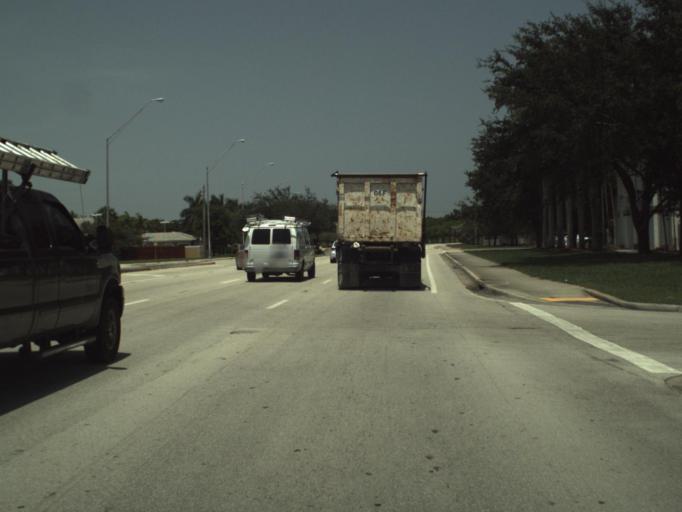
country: US
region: Florida
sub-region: Broward County
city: Coconut Creek
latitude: 26.2356
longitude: -80.1548
